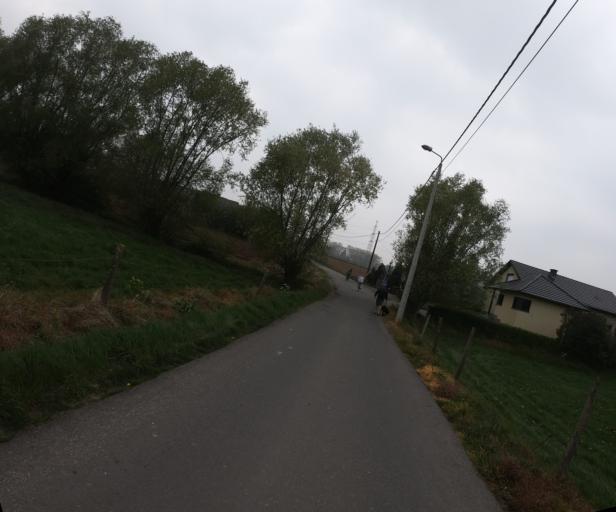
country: BE
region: Flanders
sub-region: Provincie Vlaams-Brabant
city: Halle
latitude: 50.7327
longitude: 4.2157
